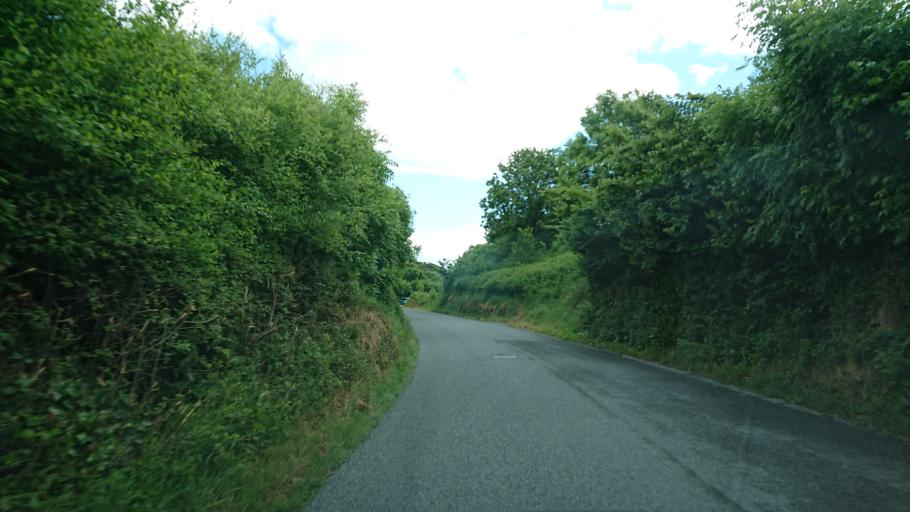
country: IE
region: Munster
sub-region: Waterford
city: Tra Mhor
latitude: 52.1764
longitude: -7.1452
